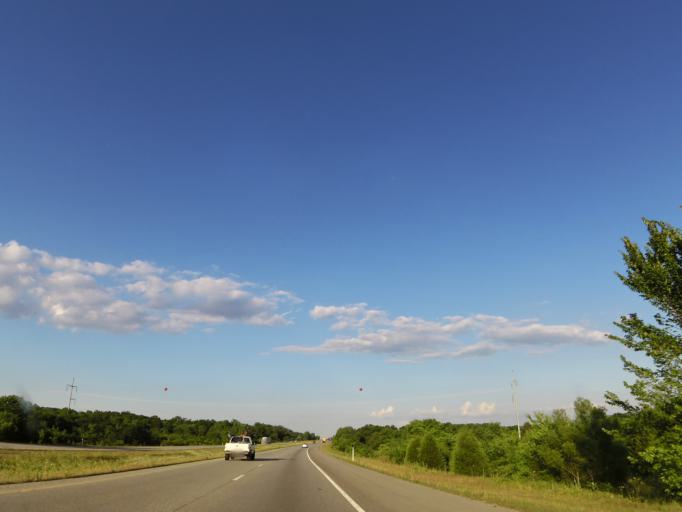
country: US
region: Tennessee
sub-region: Rutherford County
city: Smyrna
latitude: 35.8631
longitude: -86.5500
